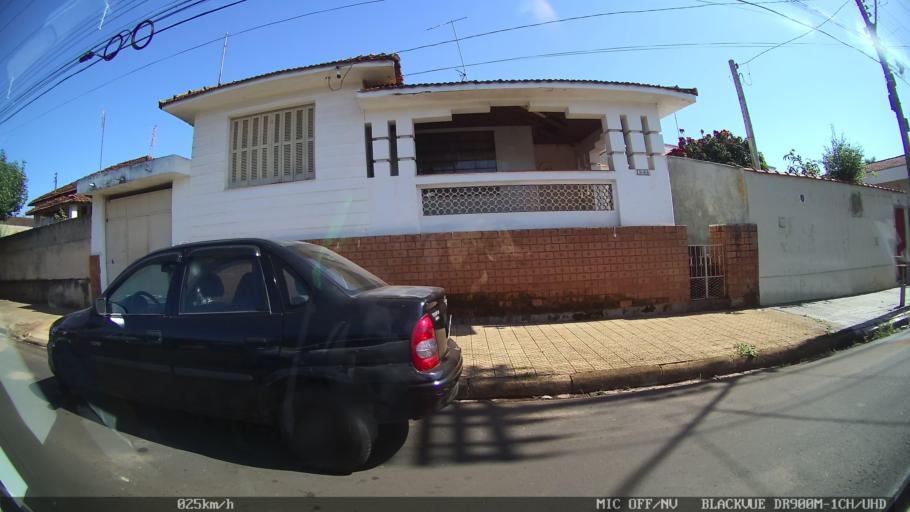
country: BR
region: Sao Paulo
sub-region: Batatais
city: Batatais
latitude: -20.8940
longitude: -47.5812
